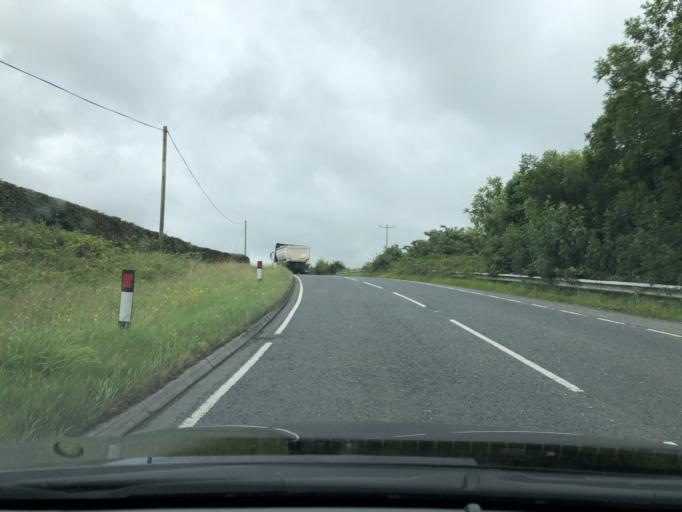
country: GB
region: Northern Ireland
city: Ballynahinch
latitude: 54.3584
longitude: -5.8577
